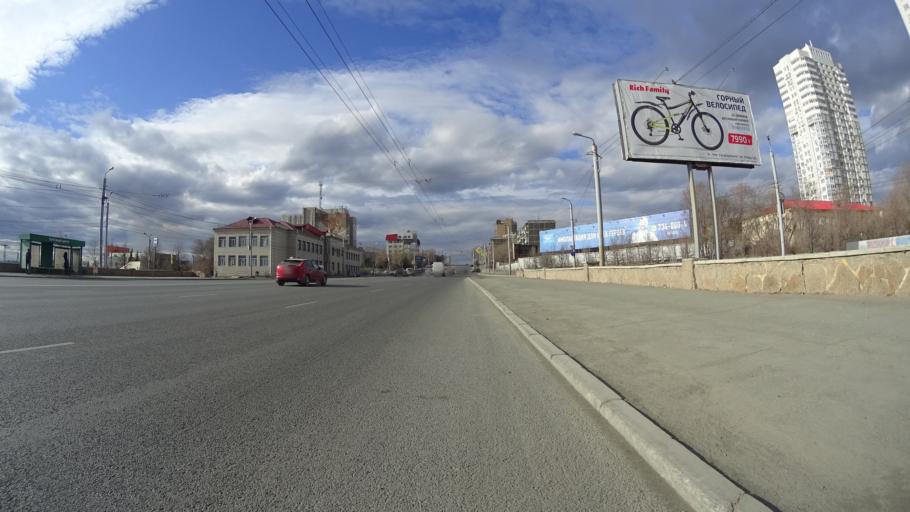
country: RU
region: Chelyabinsk
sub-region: Gorod Chelyabinsk
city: Chelyabinsk
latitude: 55.1745
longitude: 61.3879
